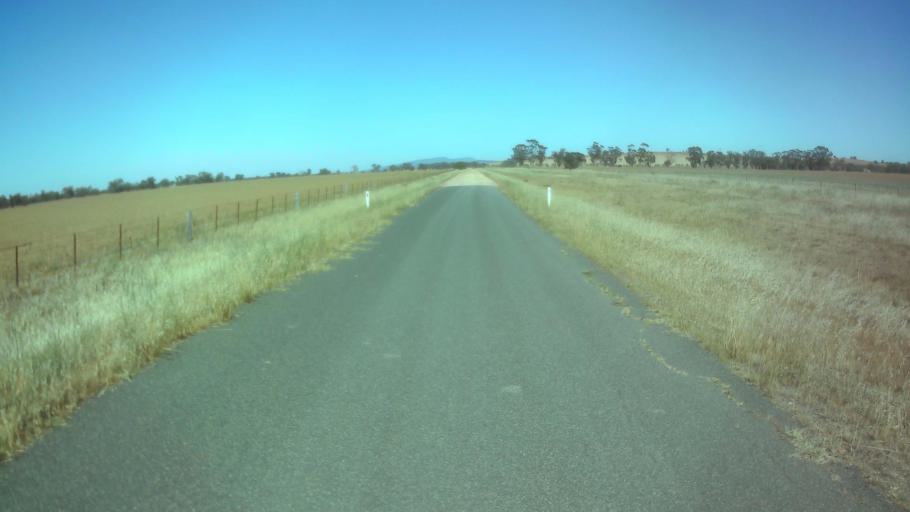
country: AU
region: New South Wales
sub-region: Weddin
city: Grenfell
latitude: -33.9964
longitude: 148.3800
